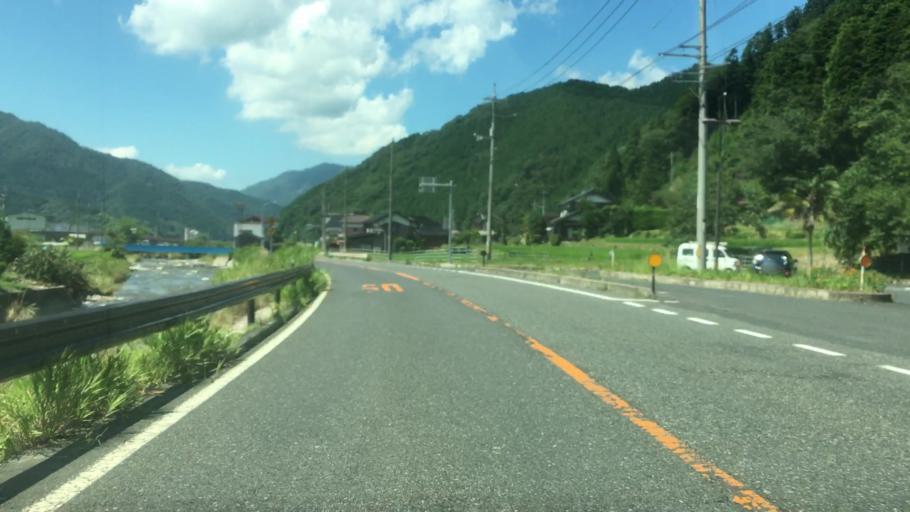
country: JP
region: Tottori
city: Tottori
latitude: 35.2494
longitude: 134.2304
